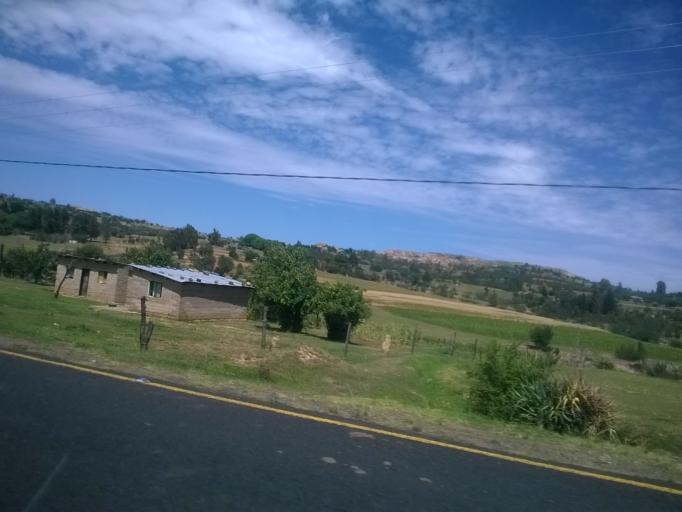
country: LS
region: Berea
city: Teyateyaneng
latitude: -29.1070
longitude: 27.8336
